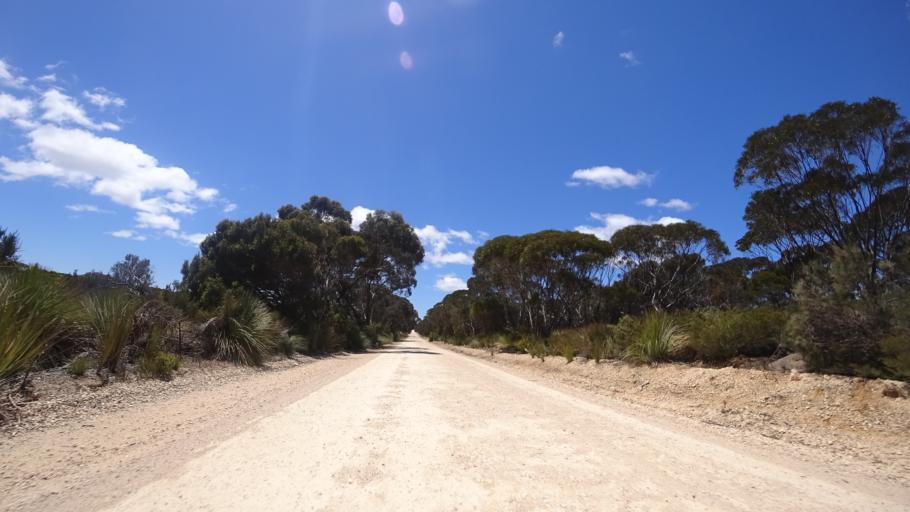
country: AU
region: South Australia
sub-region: Kangaroo Island
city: Kingscote
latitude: -35.8263
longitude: 138.0099
